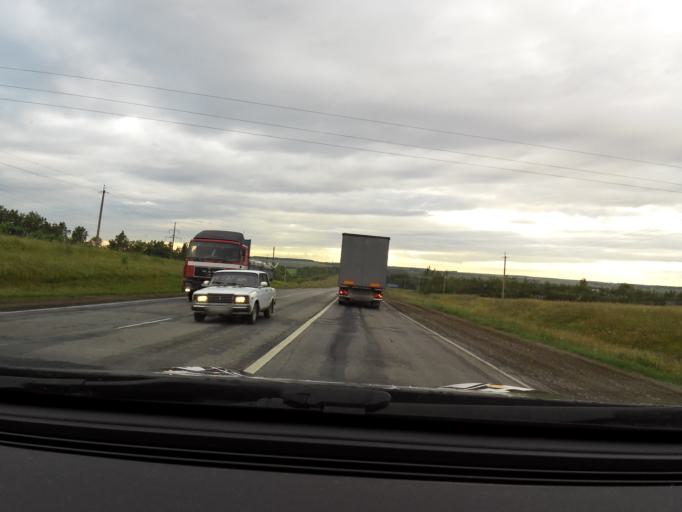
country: RU
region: Chuvashia
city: Tsivil'sk
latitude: 55.7981
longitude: 47.6485
